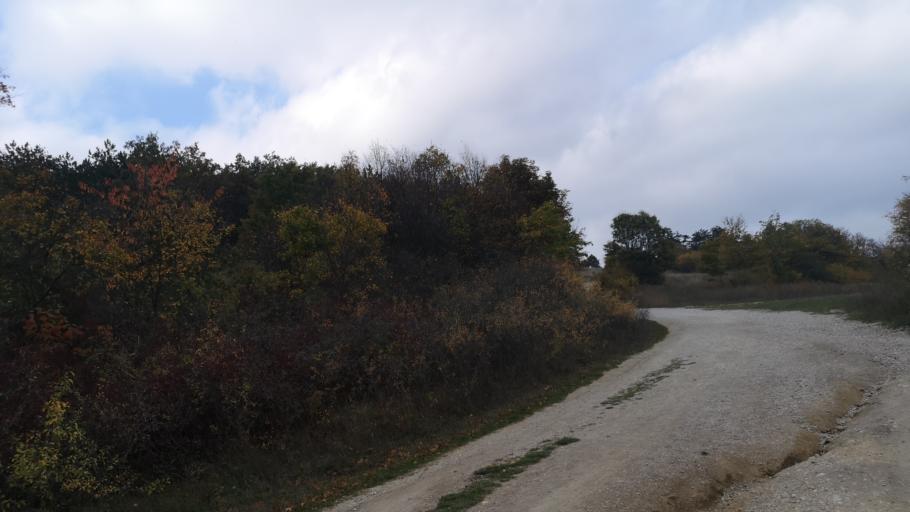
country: SK
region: Nitriansky
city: Cachtice
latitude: 48.7207
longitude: 17.7649
